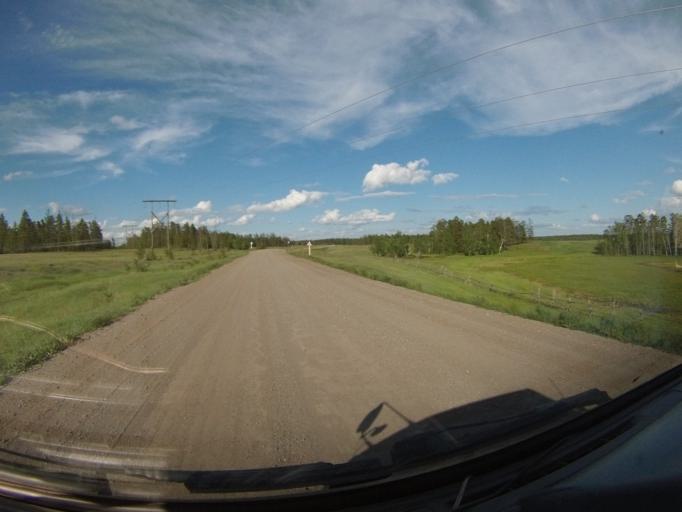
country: RU
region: Sakha
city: Ytyk-Kyuyel'
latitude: 62.2206
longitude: 133.2710
